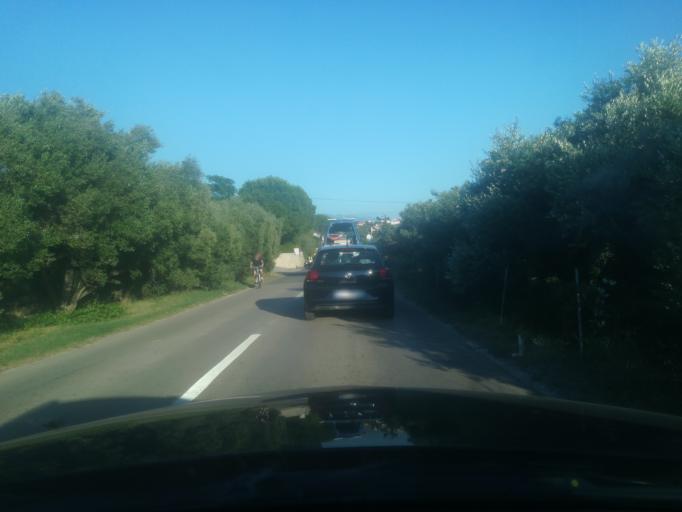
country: HR
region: Primorsko-Goranska
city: Banjol
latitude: 44.7508
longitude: 14.7845
